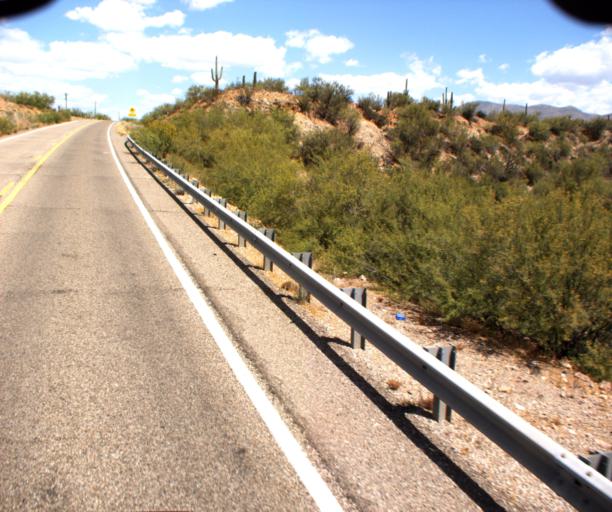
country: US
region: Arizona
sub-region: Pinal County
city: Kearny
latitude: 33.0752
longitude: -110.9216
